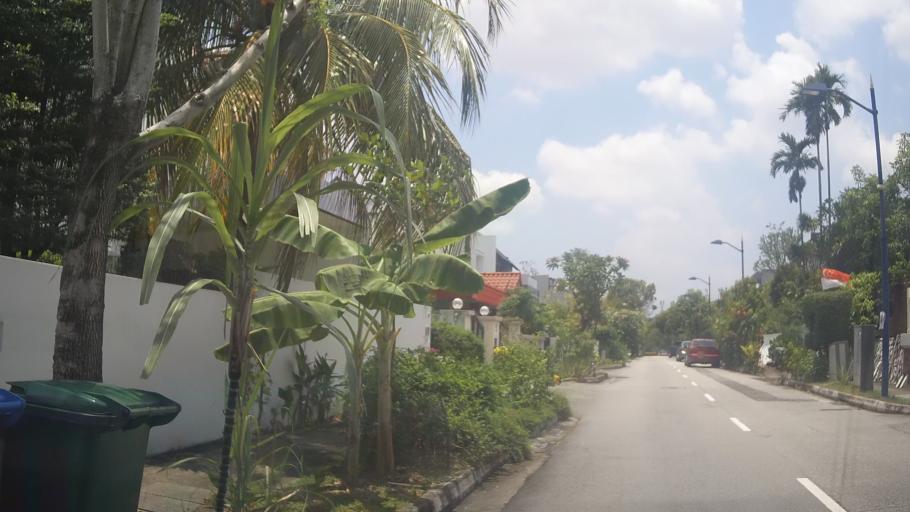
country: SG
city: Singapore
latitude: 1.3675
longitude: 103.8633
